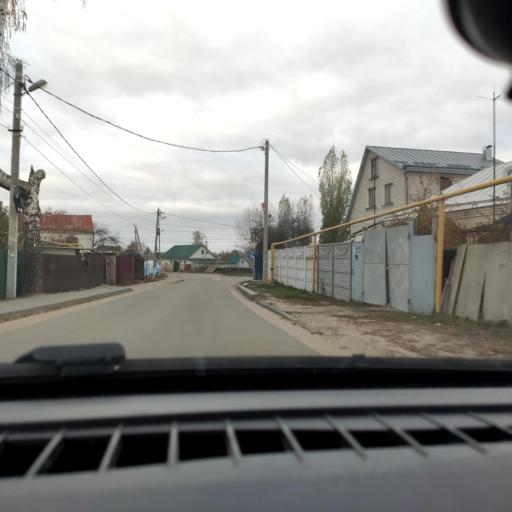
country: RU
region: Voronezj
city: Podgornoye
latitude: 51.7326
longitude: 39.1571
